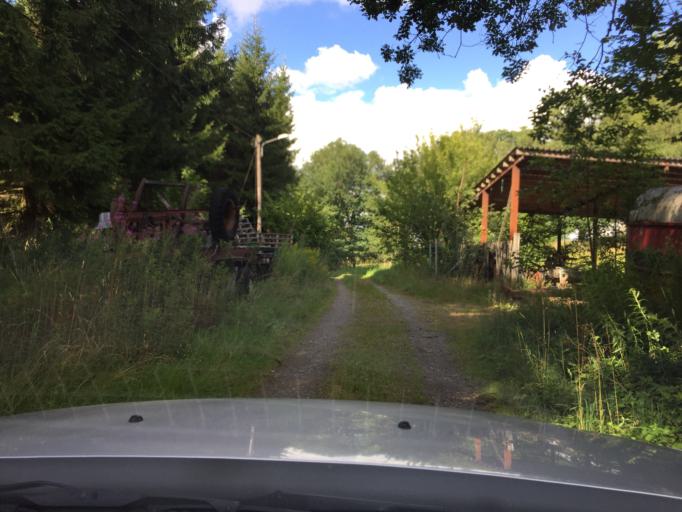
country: SE
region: Skane
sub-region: Hassleholms Kommun
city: Sosdala
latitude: 56.0305
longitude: 13.6876
